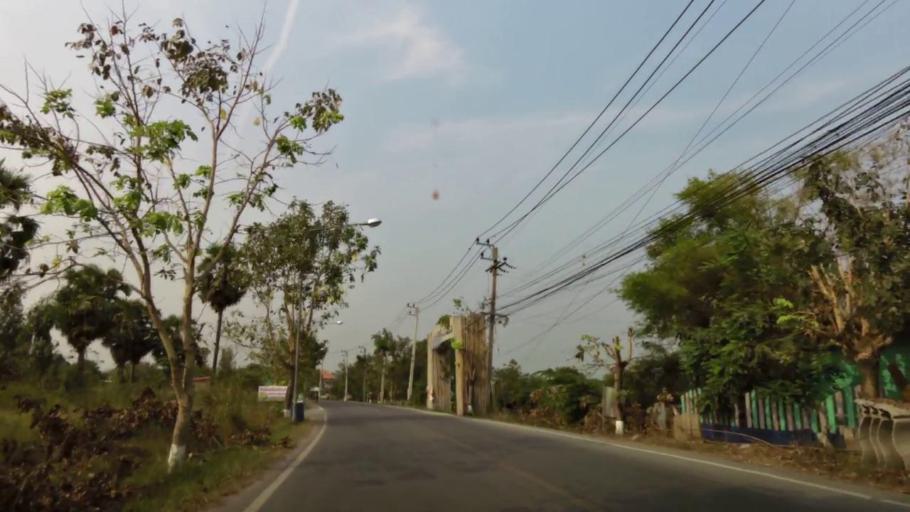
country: TH
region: Phra Nakhon Si Ayutthaya
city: Phra Nakhon Si Ayutthaya
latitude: 14.3413
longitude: 100.5742
